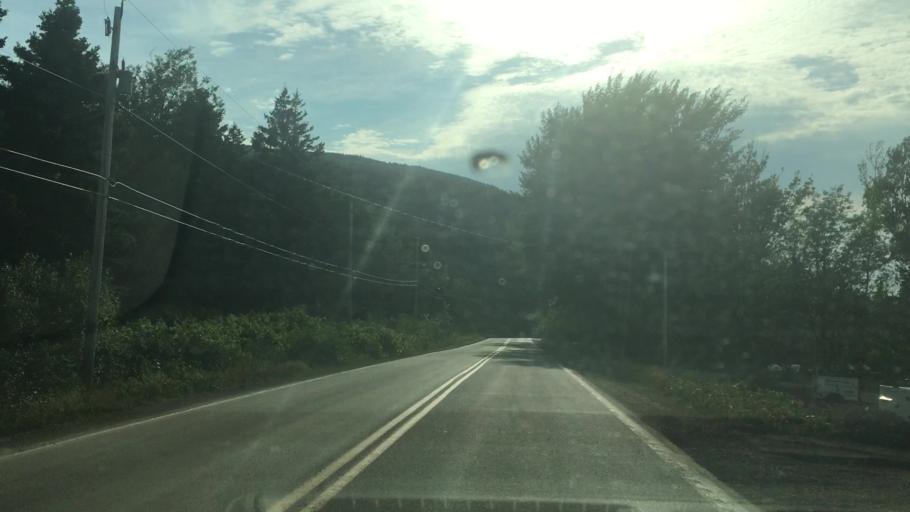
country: CA
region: Nova Scotia
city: Sydney Mines
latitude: 46.8233
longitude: -60.8238
